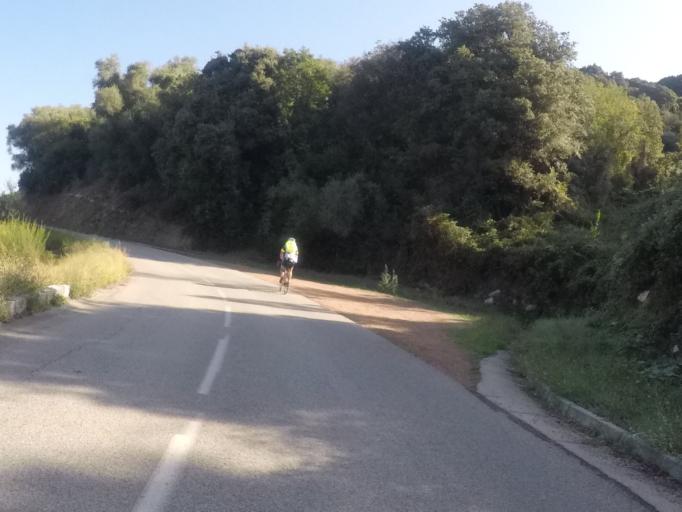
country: FR
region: Corsica
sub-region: Departement de la Corse-du-Sud
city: Olmeto
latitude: 41.7407
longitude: 8.8970
